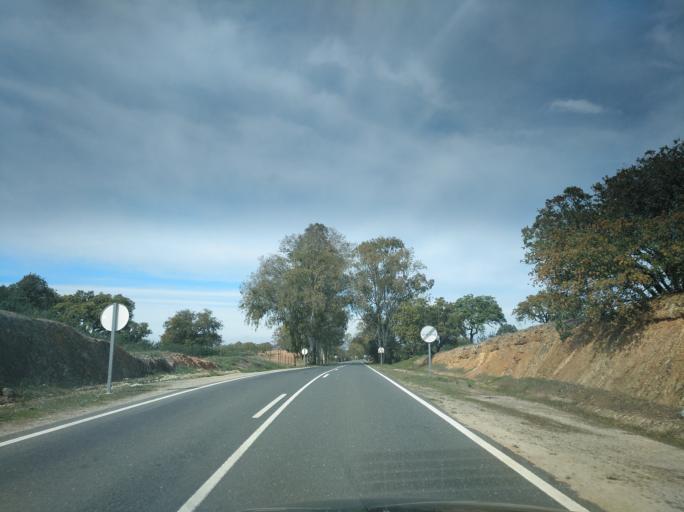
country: PT
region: Beja
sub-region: Mertola
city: Mertola
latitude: 37.7271
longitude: -7.7652
